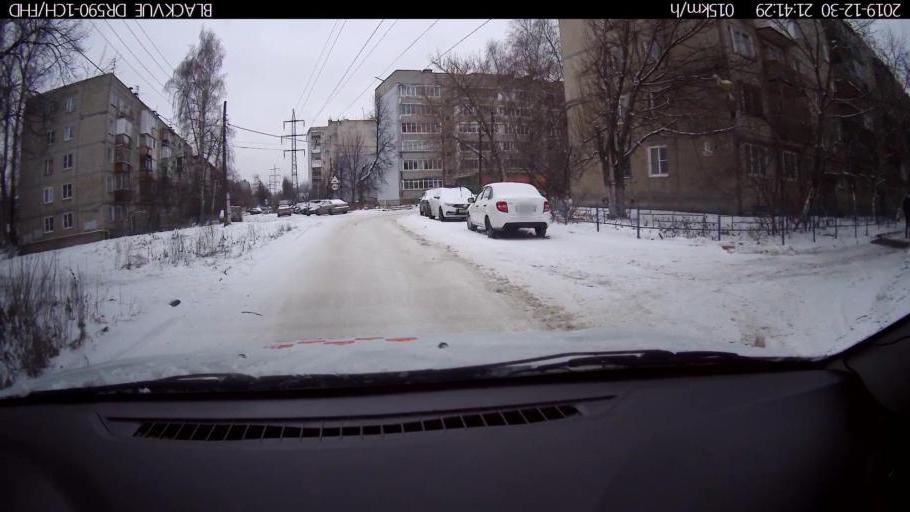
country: RU
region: Nizjnij Novgorod
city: Nizhniy Novgorod
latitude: 56.2730
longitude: 43.9292
